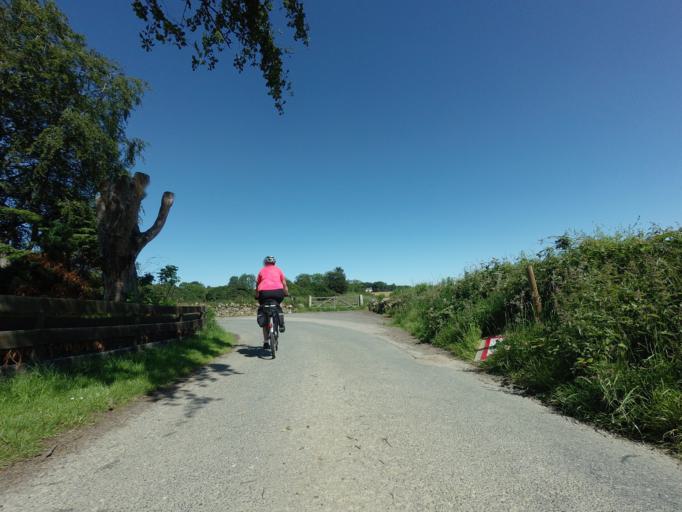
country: GB
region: Scotland
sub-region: Aberdeenshire
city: Macduff
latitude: 57.6319
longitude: -2.4847
